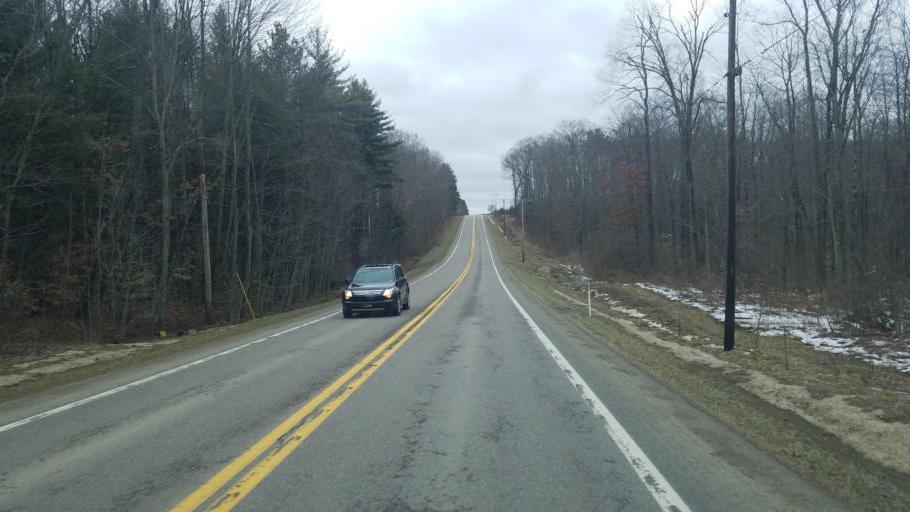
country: US
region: Pennsylvania
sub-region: Forest County
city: Marienville
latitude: 41.4033
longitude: -79.2481
